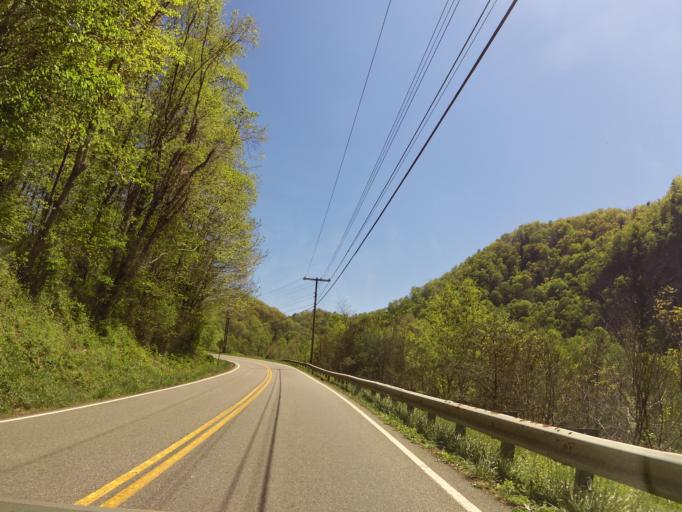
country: US
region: Tennessee
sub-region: Unicoi County
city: Banner Hill
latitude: 36.1449
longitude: -82.4412
